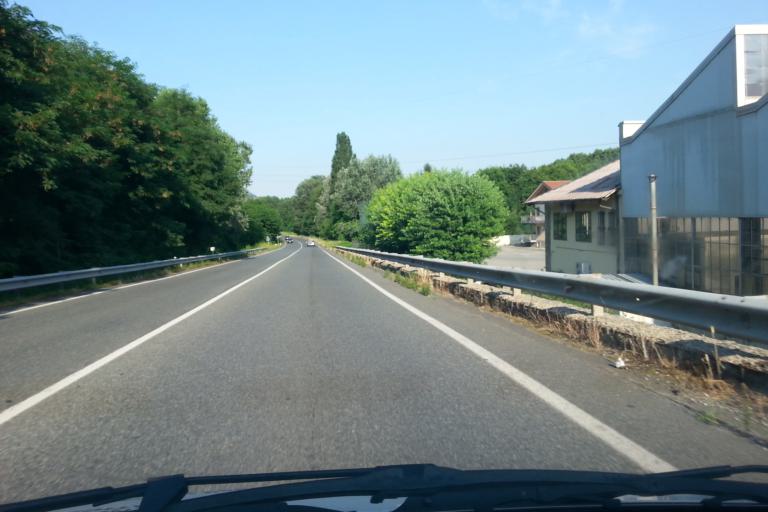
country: IT
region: Piedmont
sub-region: Provincia di Torino
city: Caprie
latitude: 45.1130
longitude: 7.3313
